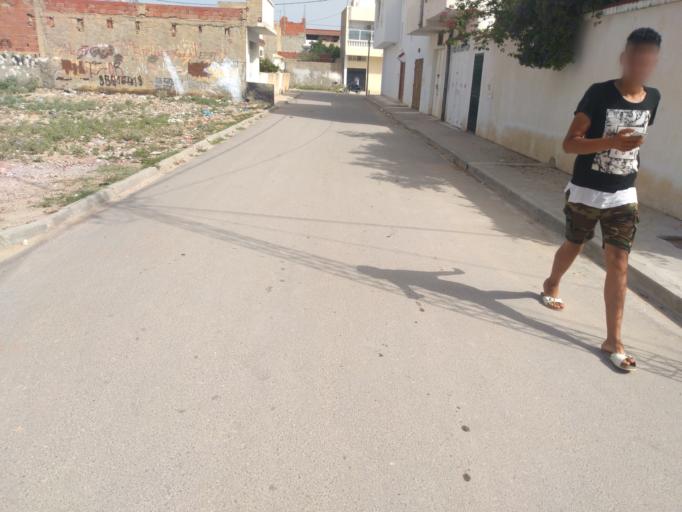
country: TN
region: Al Qayrawan
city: Kairouan
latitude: 35.6657
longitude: 10.0819
